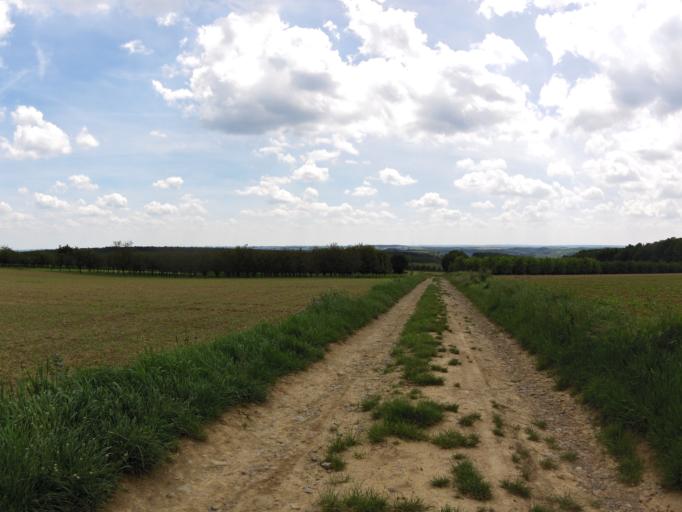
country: DE
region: Bavaria
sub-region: Regierungsbezirk Unterfranken
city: Sommerhausen
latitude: 49.7167
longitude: 10.0348
